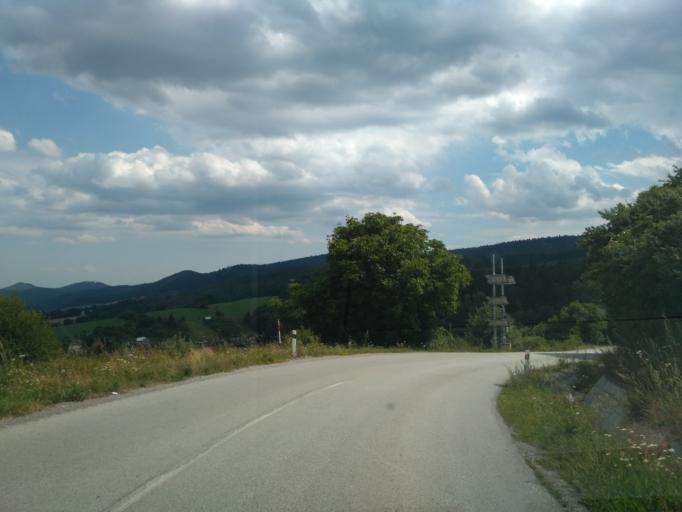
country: SK
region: Kosicky
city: Gelnica
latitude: 48.9271
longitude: 21.0490
